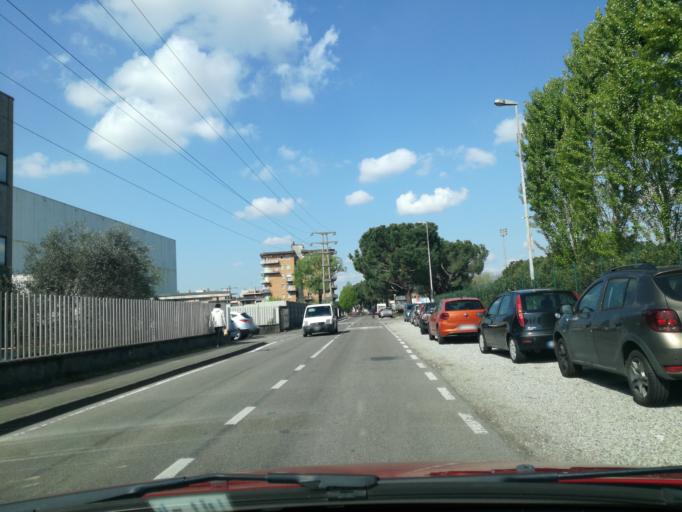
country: IT
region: Lombardy
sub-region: Provincia di Monza e Brianza
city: Limbiate
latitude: 45.5900
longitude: 9.1314
